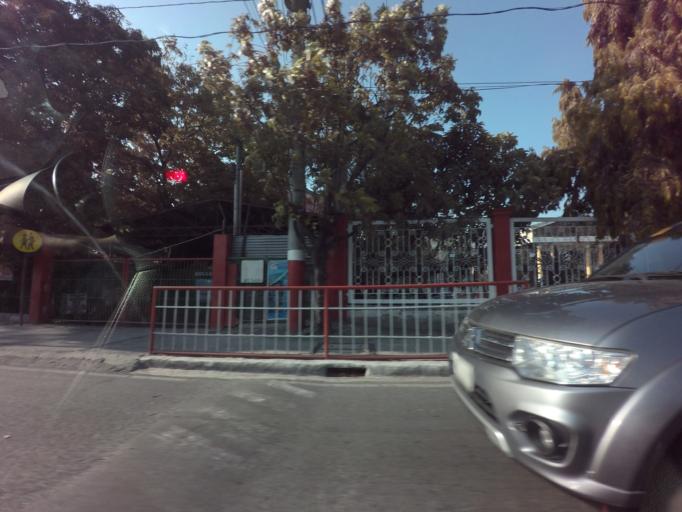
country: PH
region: Calabarzon
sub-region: Province of Rizal
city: Taguig
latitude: 14.4892
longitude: 121.0542
